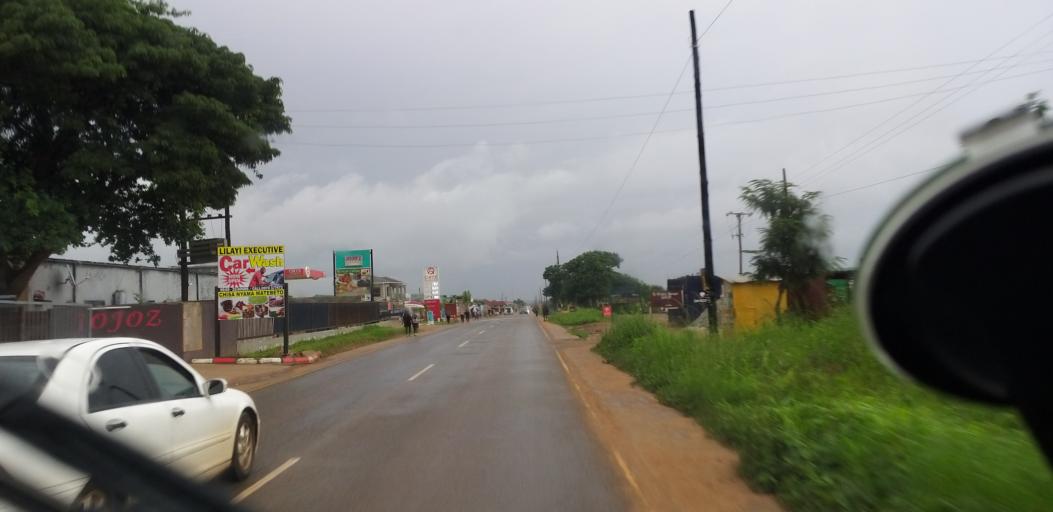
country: ZM
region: Lusaka
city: Lusaka
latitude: -15.5099
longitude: 28.3116
